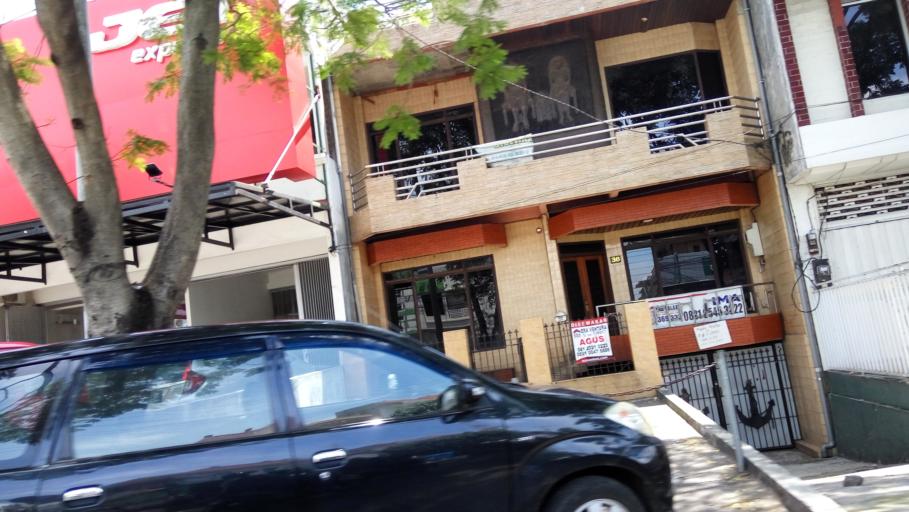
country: ID
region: East Java
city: Malang
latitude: -7.9530
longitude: 112.6389
